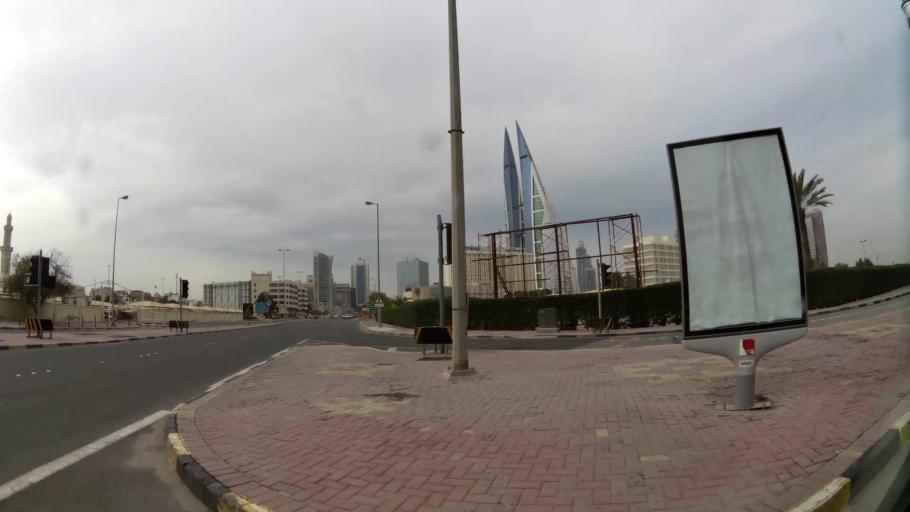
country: BH
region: Manama
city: Manama
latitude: 26.2395
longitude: 50.5870
